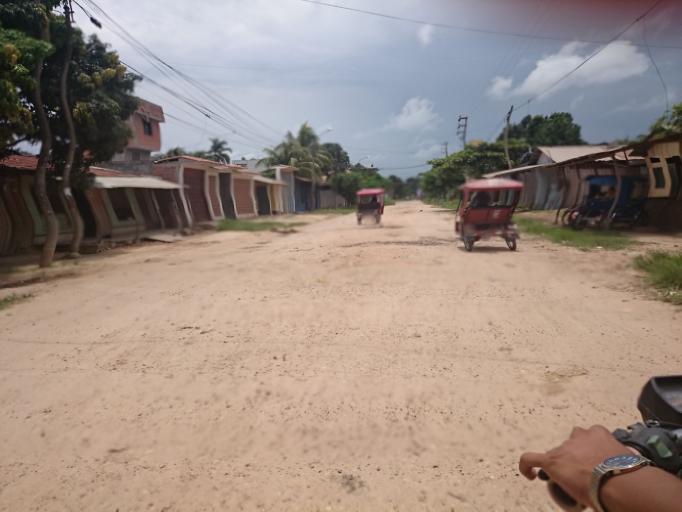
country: PE
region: Ucayali
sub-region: Provincia de Coronel Portillo
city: Pucallpa
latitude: -8.3764
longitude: -74.5597
